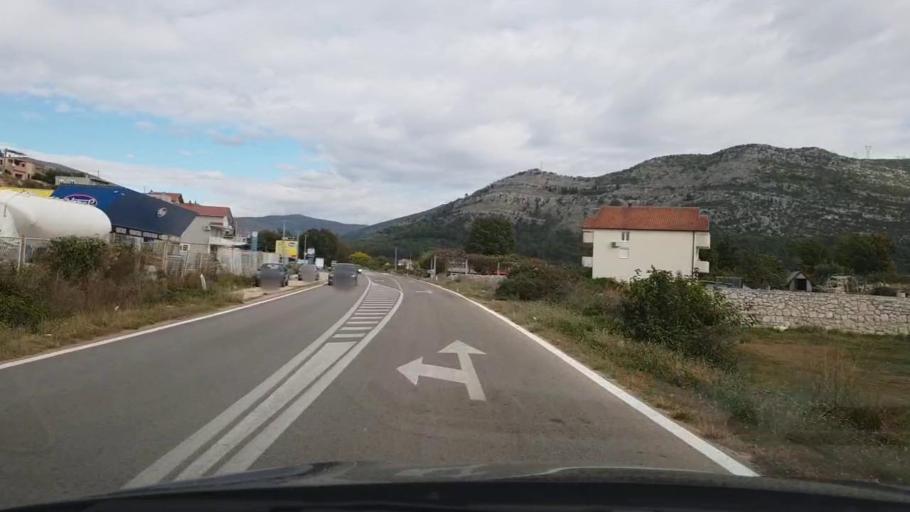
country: BA
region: Republika Srpska
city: Trebinje
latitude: 42.6856
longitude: 18.3250
